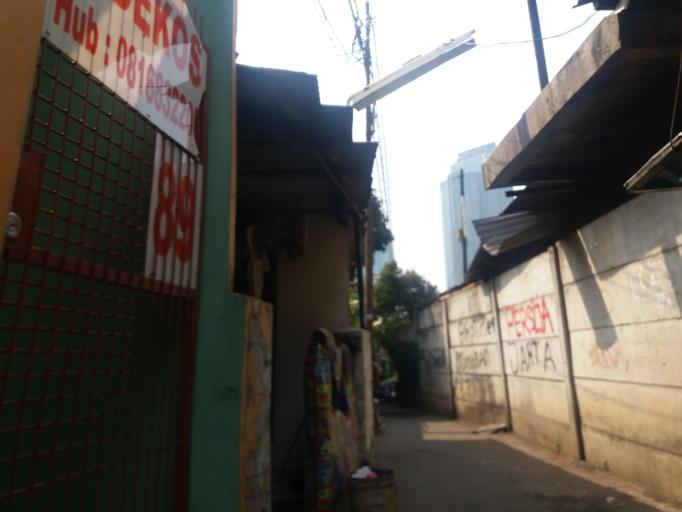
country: ID
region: Jakarta Raya
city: Jakarta
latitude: -6.2302
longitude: 106.8225
